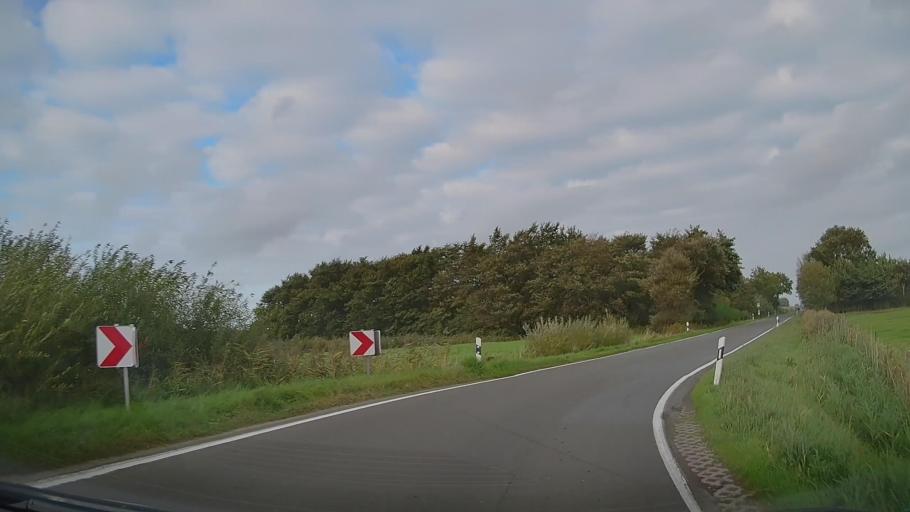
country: DE
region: Schleswig-Holstein
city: Osterhever
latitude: 54.3959
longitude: 8.7578
